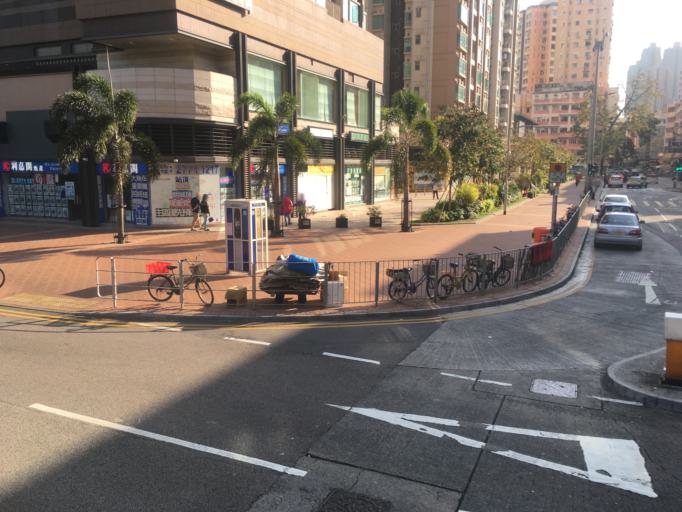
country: HK
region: Yuen Long
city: Yuen Long Kau Hui
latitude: 22.4461
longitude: 114.0273
